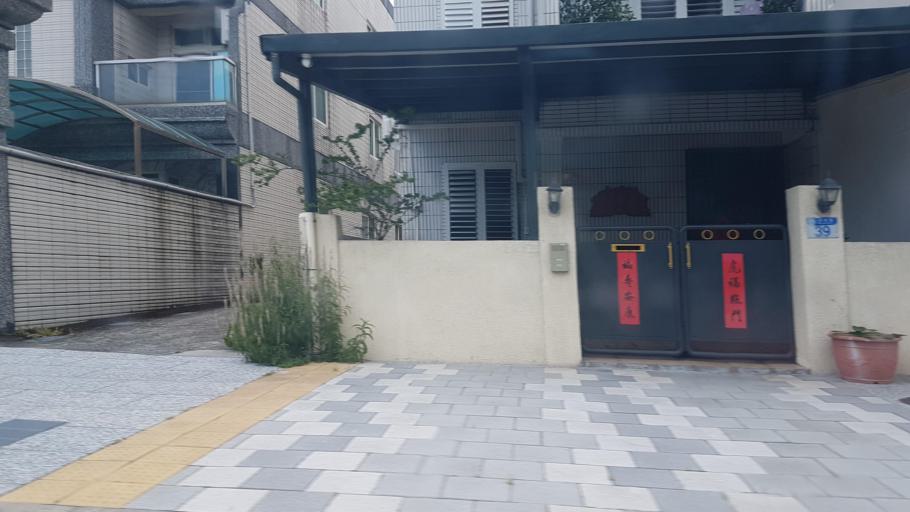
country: TW
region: Taiwan
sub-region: Hualien
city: Hualian
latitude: 23.9949
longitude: 121.6334
